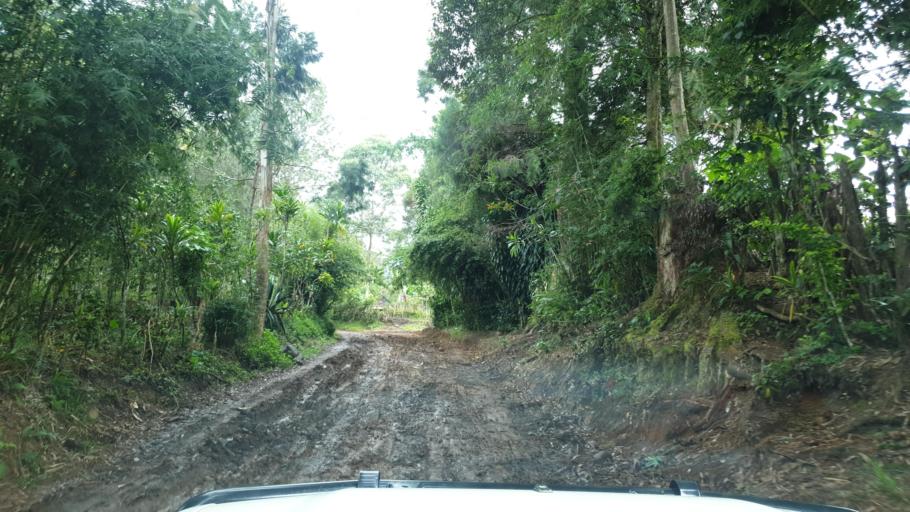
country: PG
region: Eastern Highlands
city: Goroka
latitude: -5.9201
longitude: 145.2608
